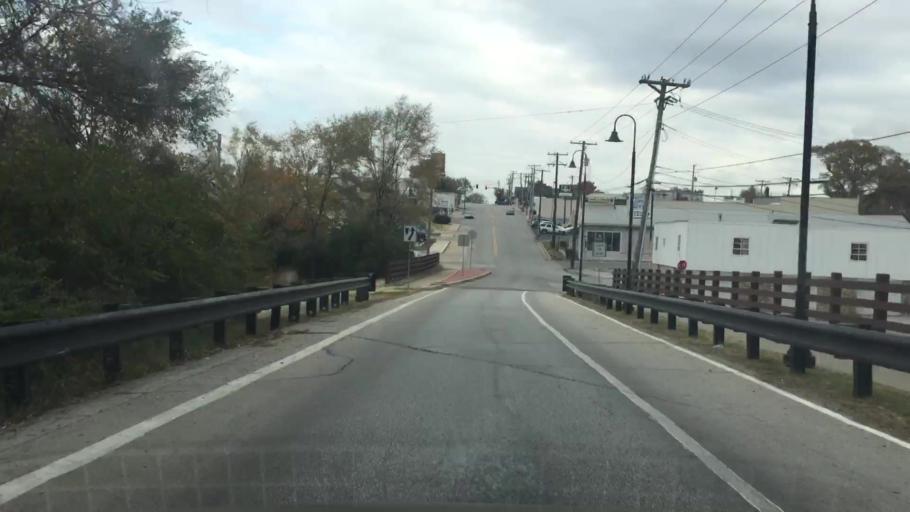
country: US
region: Missouri
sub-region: Jackson County
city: Raytown
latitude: 39.0061
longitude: -94.4636
